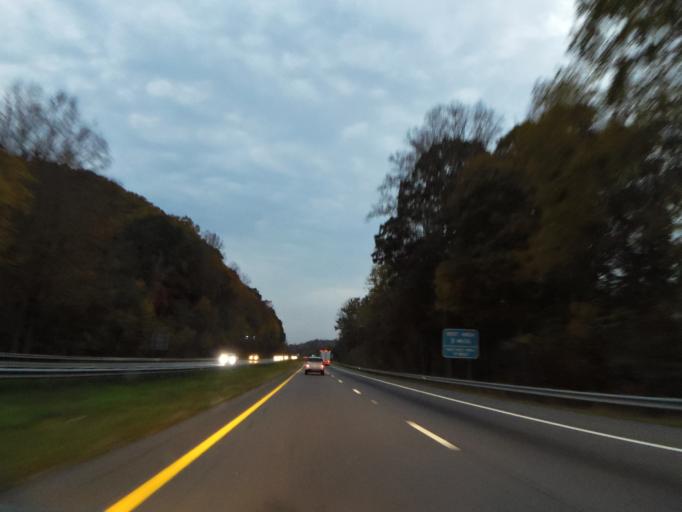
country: US
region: North Carolina
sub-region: McDowell County
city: Marion
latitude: 35.6516
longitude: -81.9734
